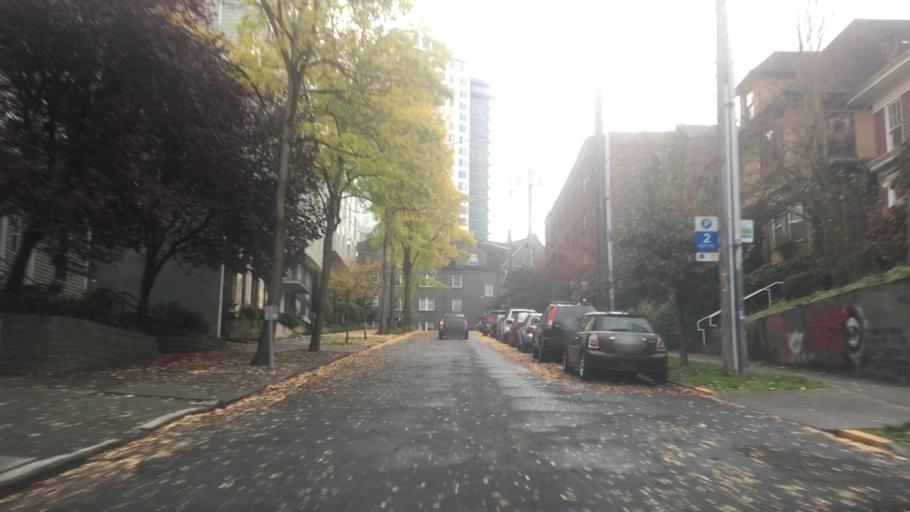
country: US
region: Washington
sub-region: King County
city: Seattle
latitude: 47.6139
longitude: -122.3234
